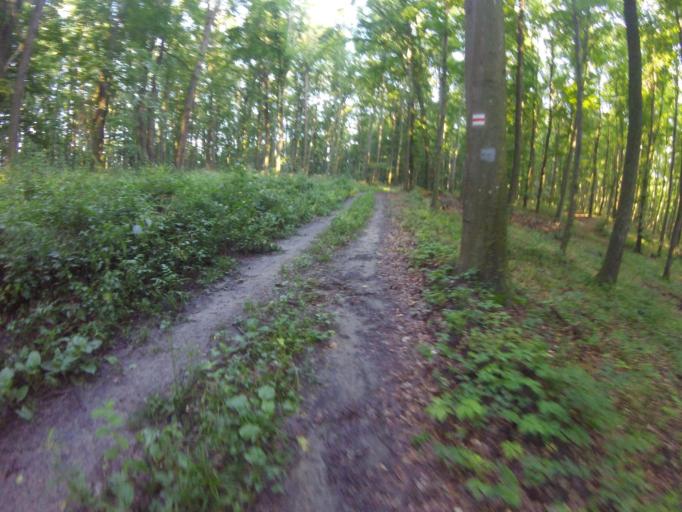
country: HU
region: Zala
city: Letenye
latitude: 46.5167
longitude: 16.7276
